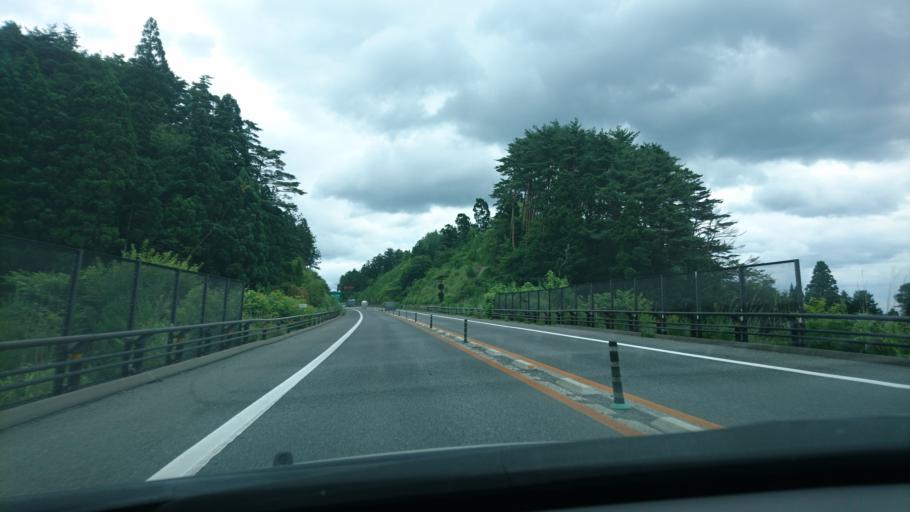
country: JP
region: Iwate
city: Ofunato
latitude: 39.0286
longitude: 141.7057
